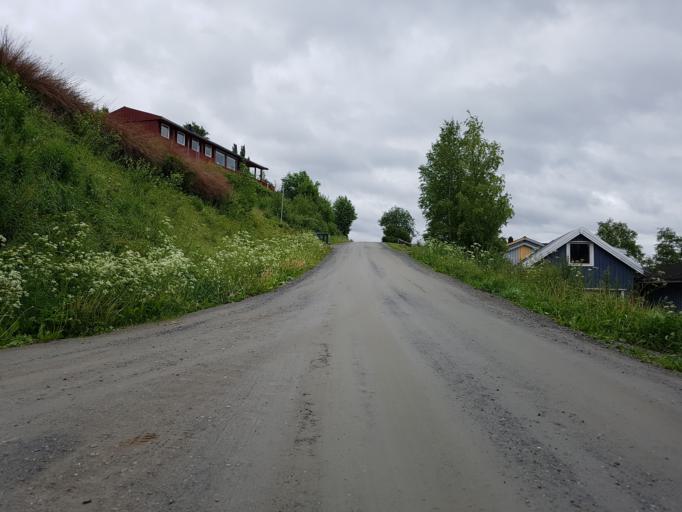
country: NO
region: Sor-Trondelag
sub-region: Selbu
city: Mebonden
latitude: 63.2255
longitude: 11.0359
